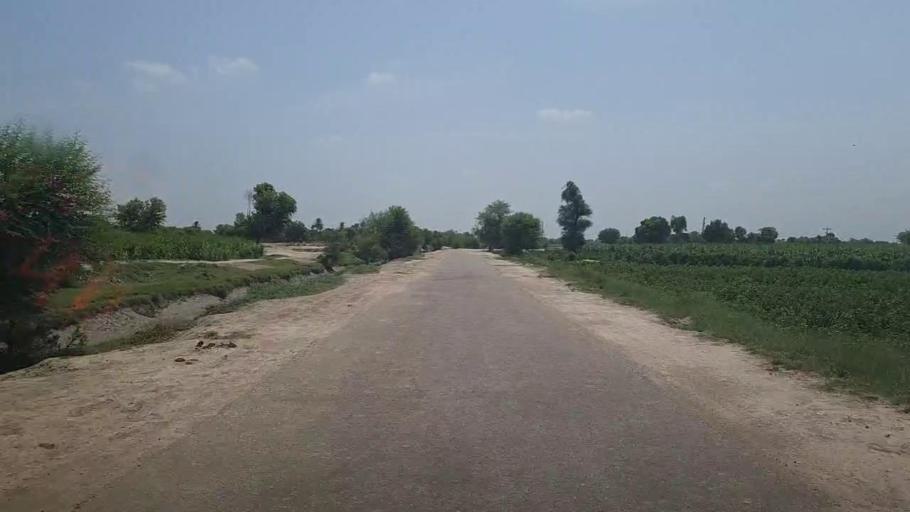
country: PK
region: Sindh
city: Ubauro
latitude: 28.2918
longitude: 69.8074
